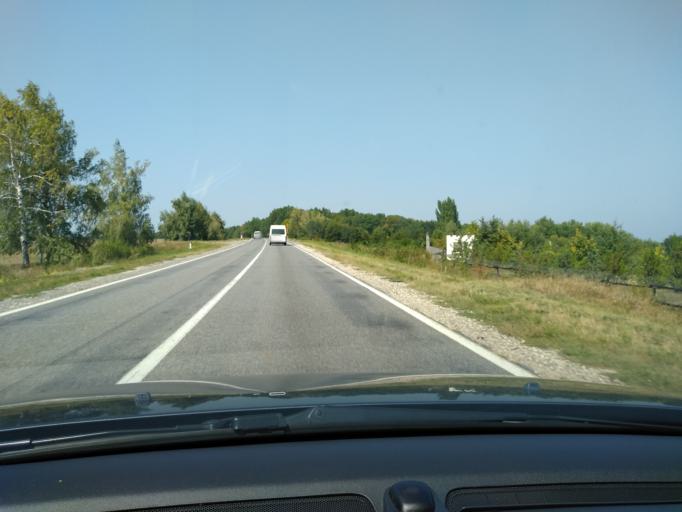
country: MD
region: Stinga Nistrului
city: Bucovat
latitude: 47.1160
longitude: 28.4699
